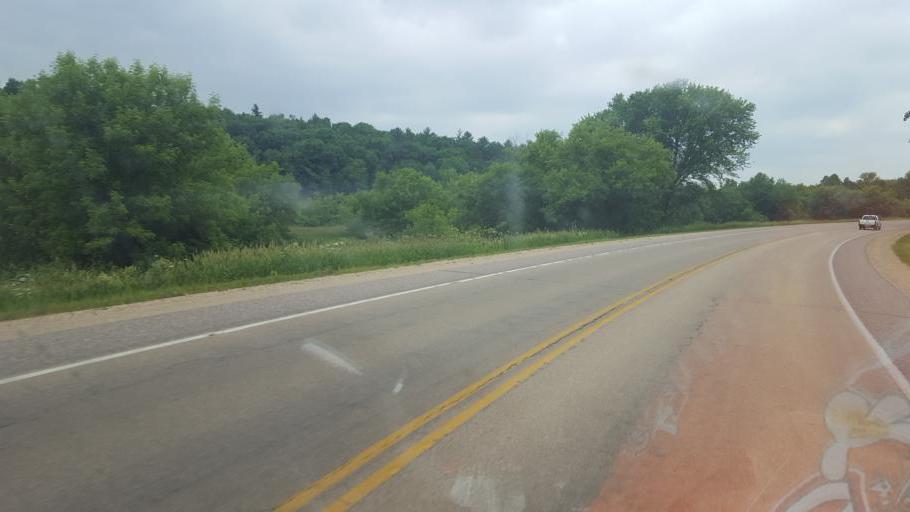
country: US
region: Wisconsin
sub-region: Juneau County
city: Elroy
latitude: 43.6402
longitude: -90.2066
